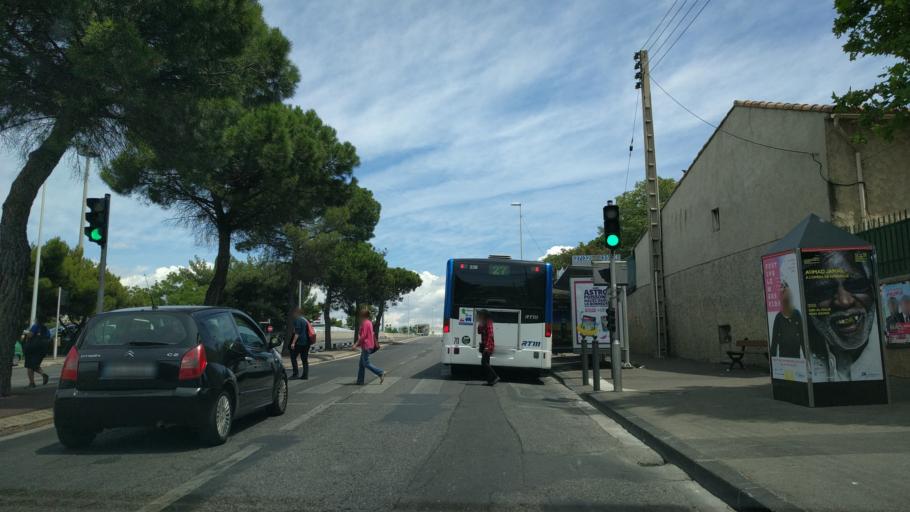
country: FR
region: Provence-Alpes-Cote d'Azur
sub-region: Departement des Bouches-du-Rhone
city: Marseille 13
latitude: 43.3285
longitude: 5.3995
